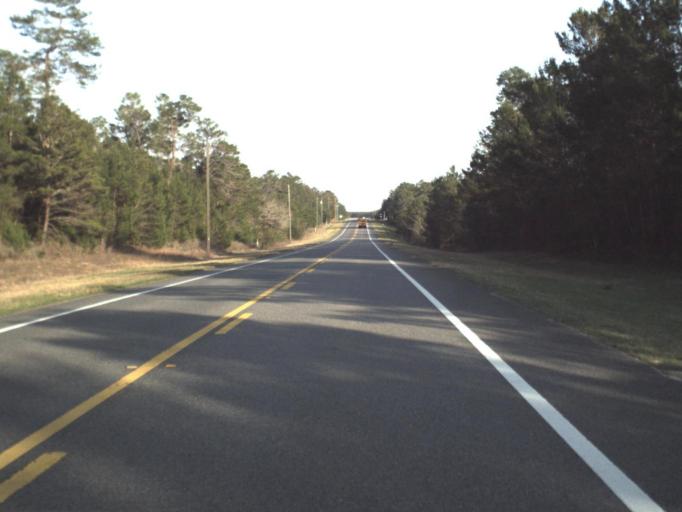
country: US
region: Florida
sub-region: Bay County
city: Lynn Haven
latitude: 30.4278
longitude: -85.6734
